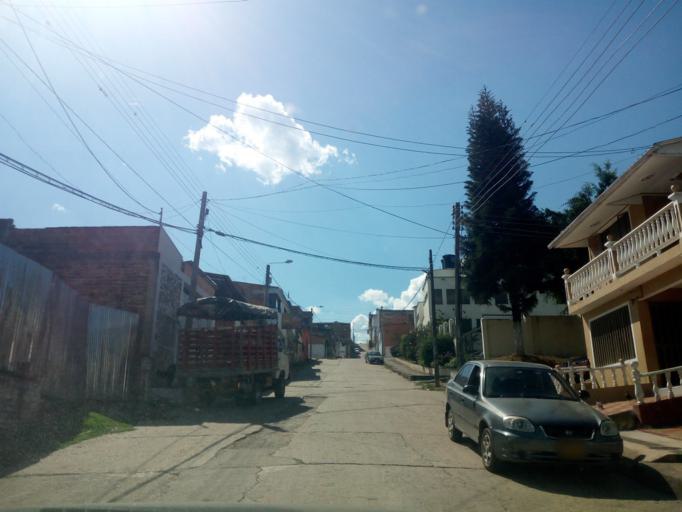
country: CO
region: Boyaca
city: Guateque
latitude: 5.0050
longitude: -73.4709
